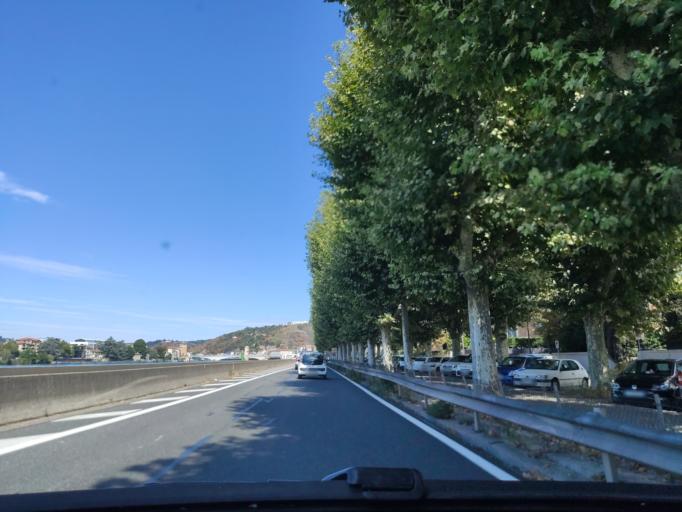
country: FR
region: Rhone-Alpes
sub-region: Departement de l'Isere
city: Vienne
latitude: 45.5180
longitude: 4.8649
